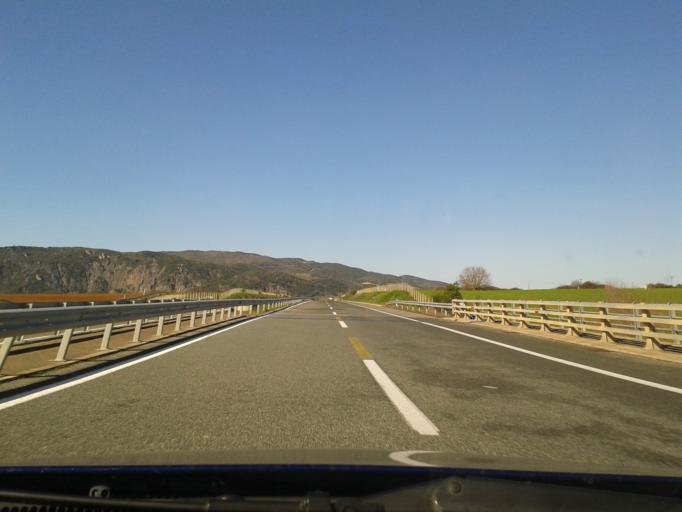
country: GR
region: West Greece
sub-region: Nomos Aitolias kai Akarnanias
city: Fitiai
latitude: 38.6671
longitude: 21.2367
